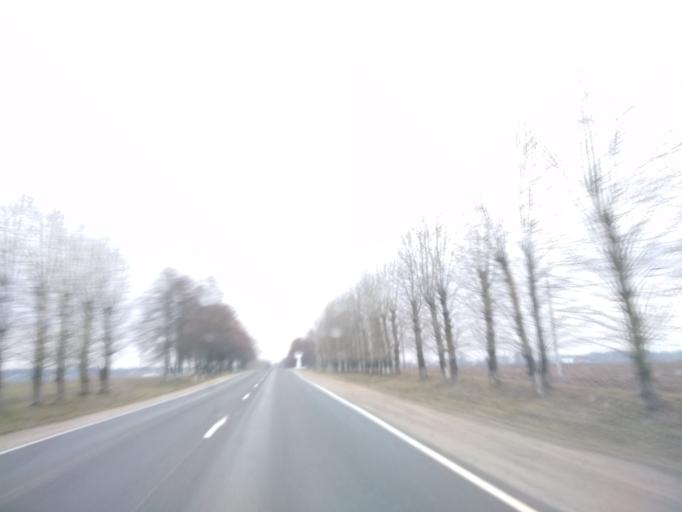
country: BY
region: Minsk
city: Blon'
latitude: 53.5340
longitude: 28.1547
